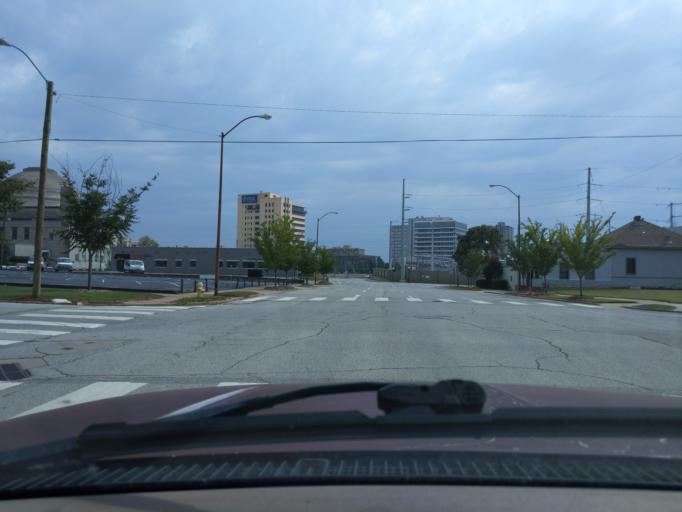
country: US
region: Oklahoma
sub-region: Tulsa County
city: Tulsa
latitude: 36.1469
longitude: -95.9904
